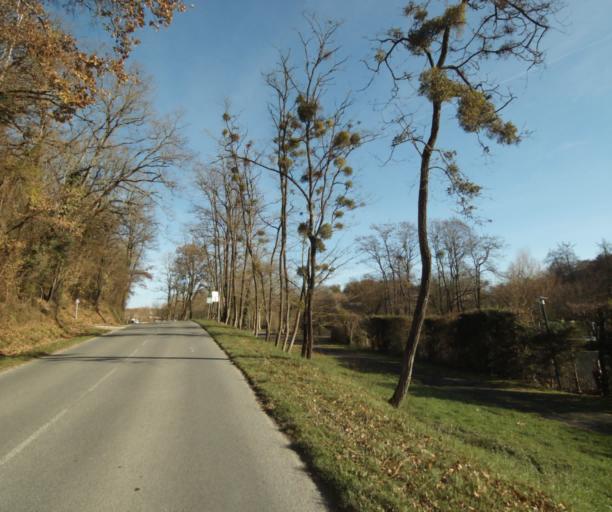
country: FR
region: Poitou-Charentes
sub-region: Departement de la Charente-Maritime
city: Ecoyeux
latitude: 45.7630
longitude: -0.4976
